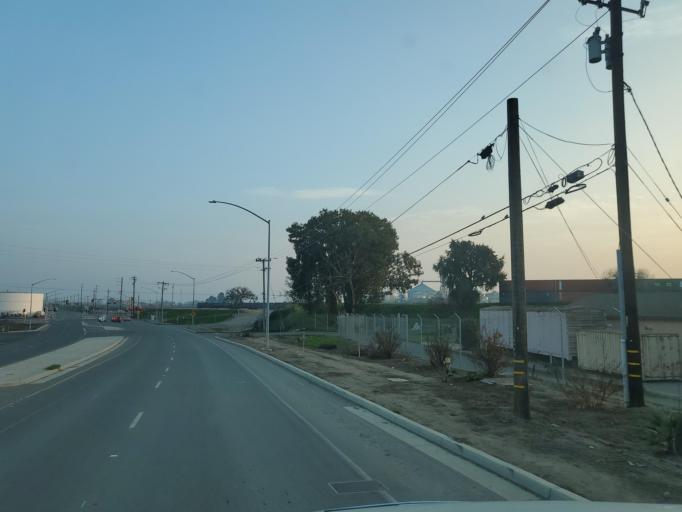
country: US
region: California
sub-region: San Joaquin County
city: Country Club
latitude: 37.9460
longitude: -121.3383
